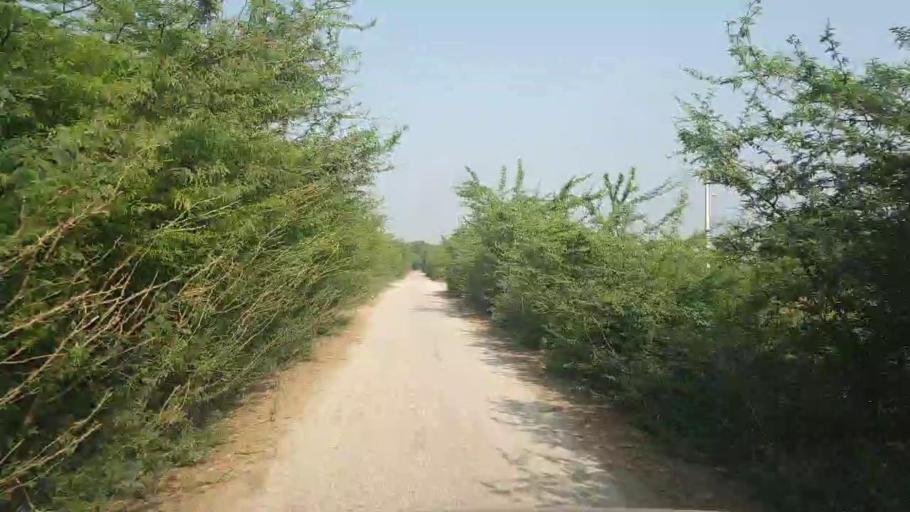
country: PK
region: Sindh
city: Umarkot
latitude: 25.3782
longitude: 69.7291
